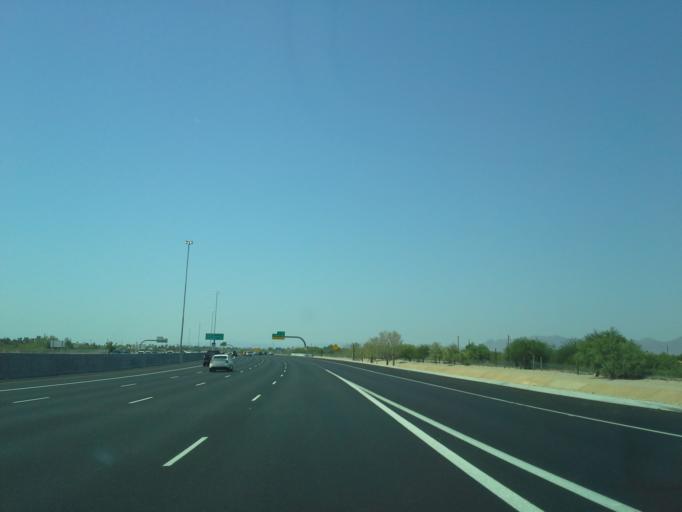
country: US
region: Arizona
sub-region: Maricopa County
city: Scottsdale
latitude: 33.4704
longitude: -111.8879
